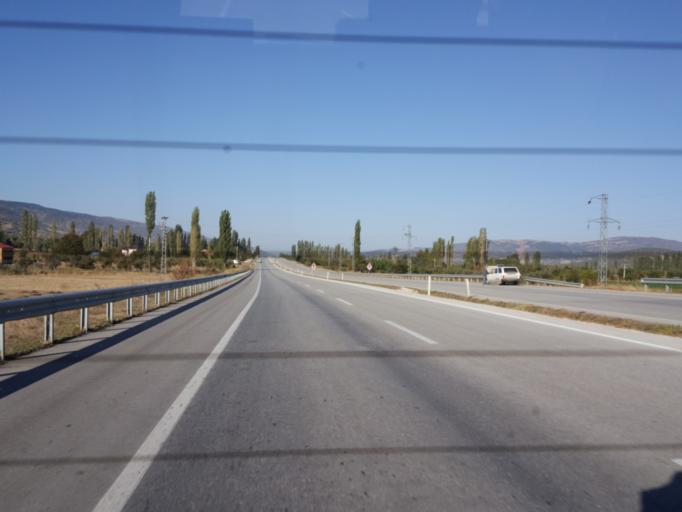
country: TR
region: Amasya
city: Ezinepazari
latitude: 40.5721
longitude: 36.1150
